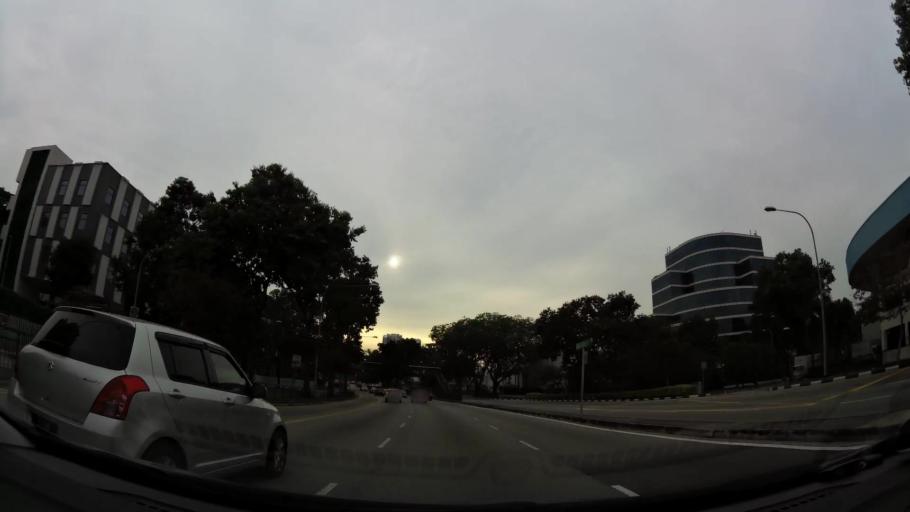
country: SG
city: Singapore
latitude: 1.3716
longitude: 103.8667
